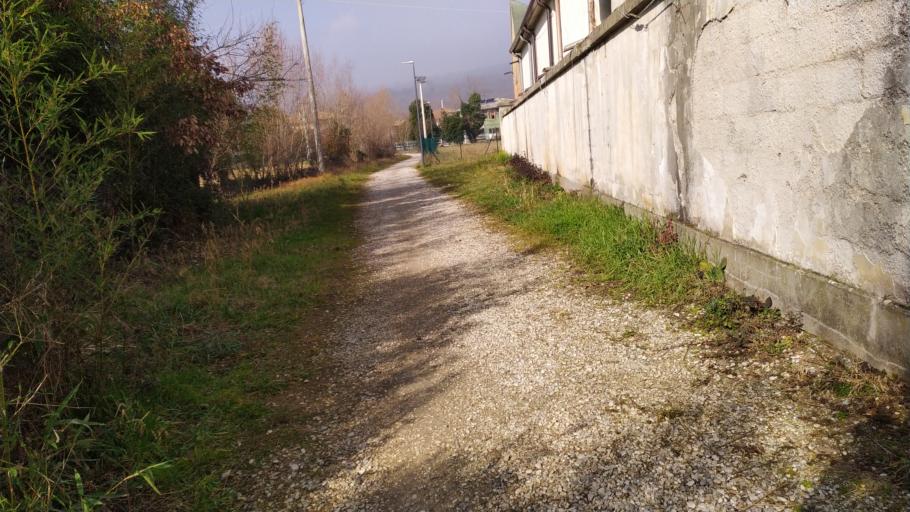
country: IT
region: Veneto
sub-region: Provincia di Treviso
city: Volpago del Montello
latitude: 45.7793
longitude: 12.1158
